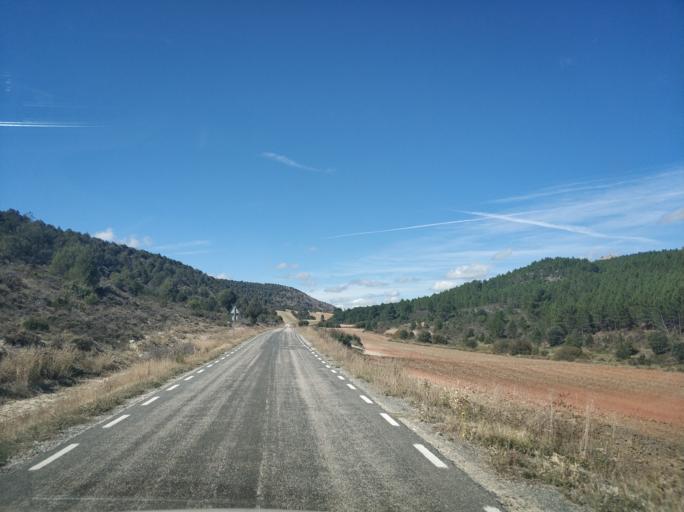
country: ES
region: Castille and Leon
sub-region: Provincia de Soria
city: Espeja de San Marcelino
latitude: 41.8143
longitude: -3.2294
